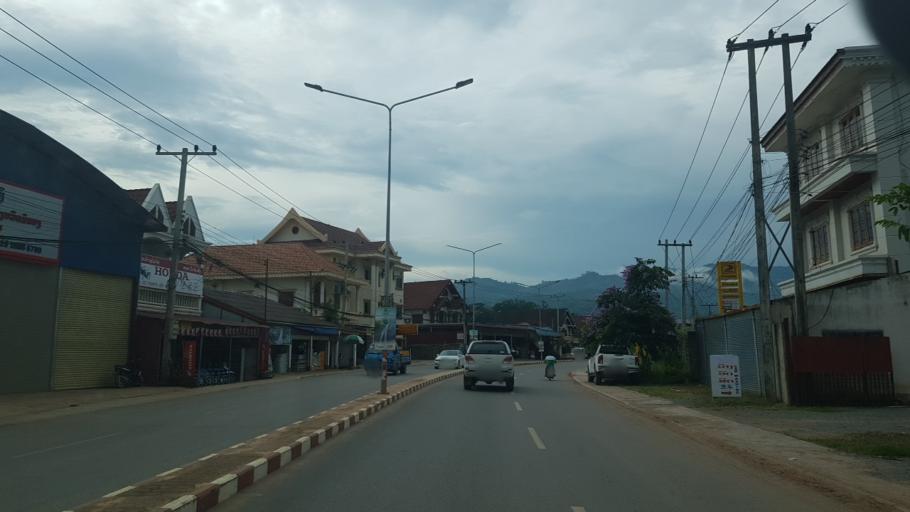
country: LA
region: Oudomxai
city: Muang Xay
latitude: 20.6801
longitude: 101.9864
